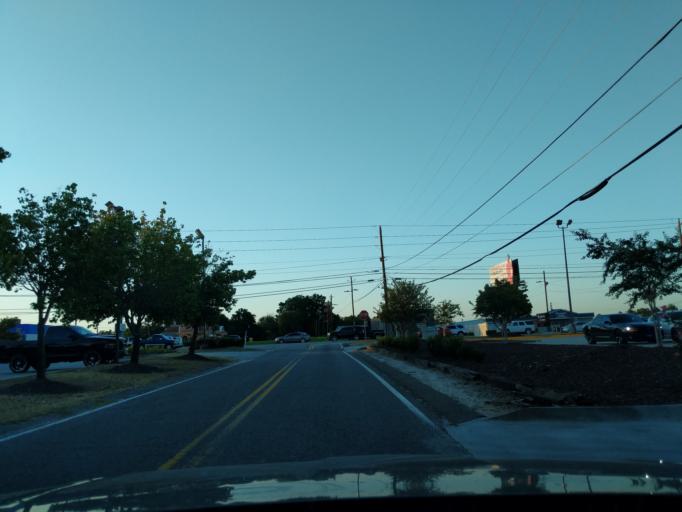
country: US
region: Georgia
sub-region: Columbia County
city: Martinez
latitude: 33.5105
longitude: -82.0931
